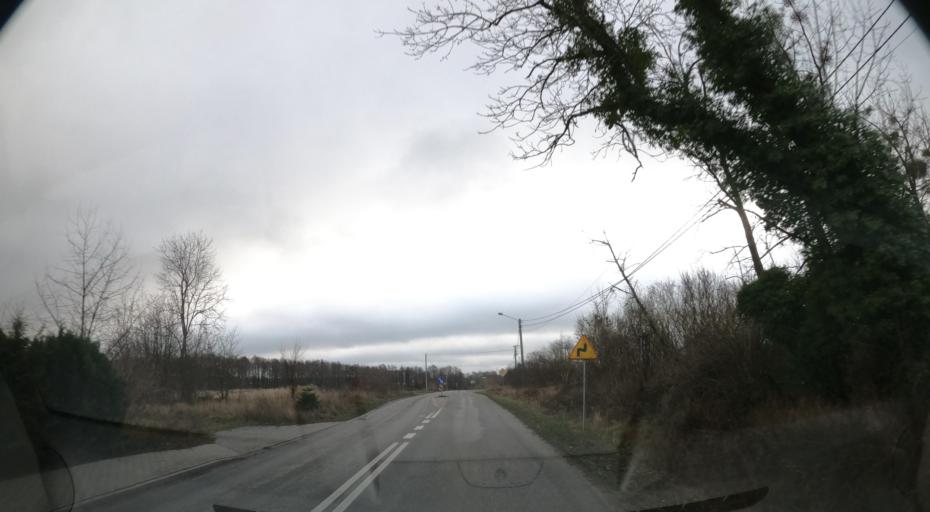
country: PL
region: Kujawsko-Pomorskie
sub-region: Powiat nakielski
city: Sadki
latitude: 53.1915
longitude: 17.3927
